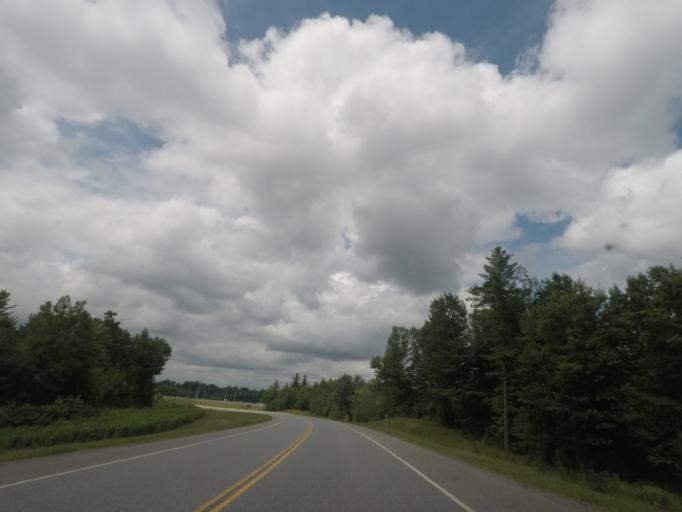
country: US
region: New York
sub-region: Saratoga County
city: Country Knolls
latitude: 42.9601
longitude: -73.7515
